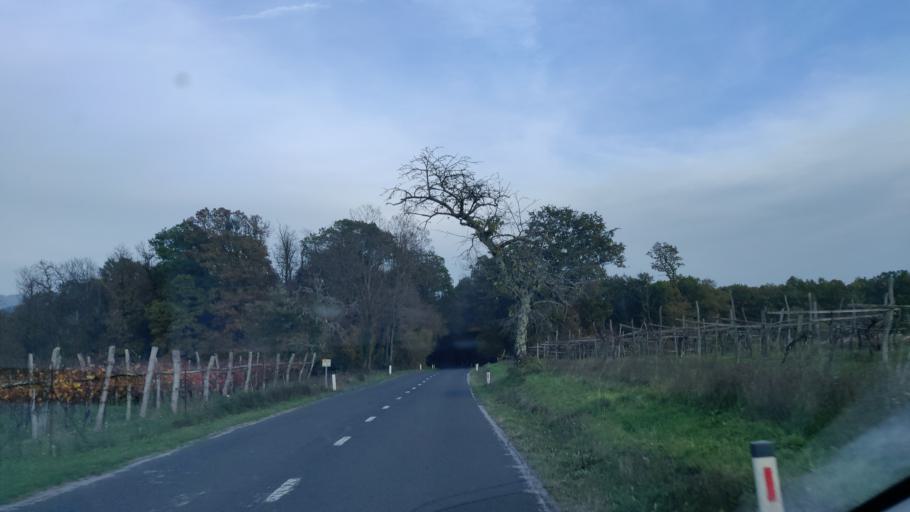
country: SI
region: Sezana
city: Sezana
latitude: 45.7663
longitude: 13.8878
